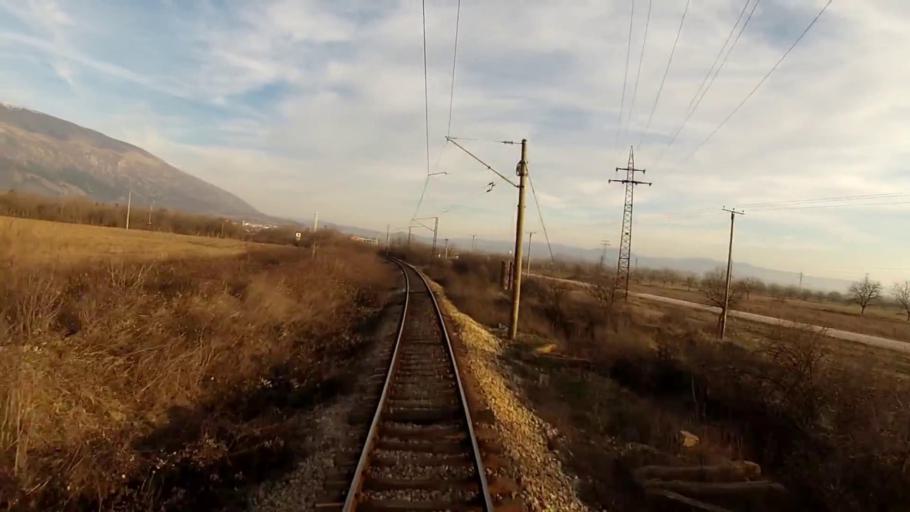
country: BG
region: Plovdiv
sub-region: Obshtina Karlovo
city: Karlovo
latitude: 42.6318
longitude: 24.7784
